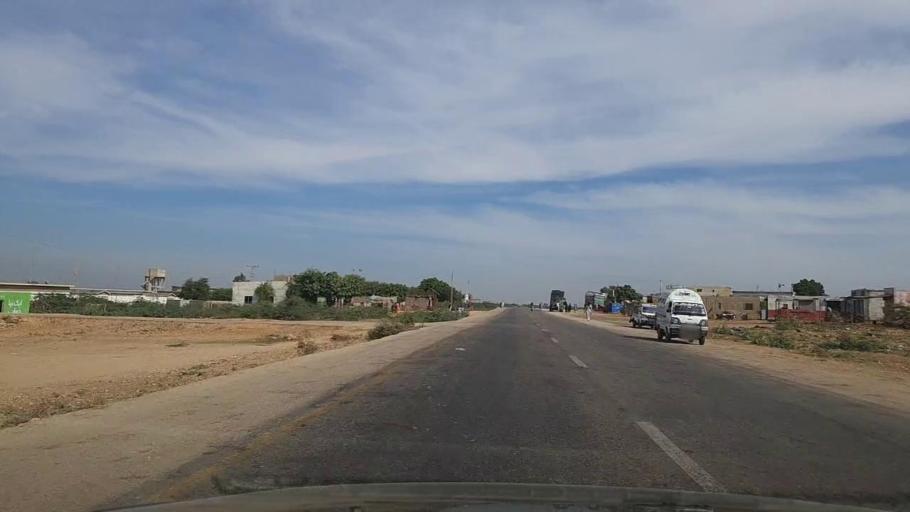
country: PK
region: Sindh
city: Thatta
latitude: 24.8352
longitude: 68.0000
